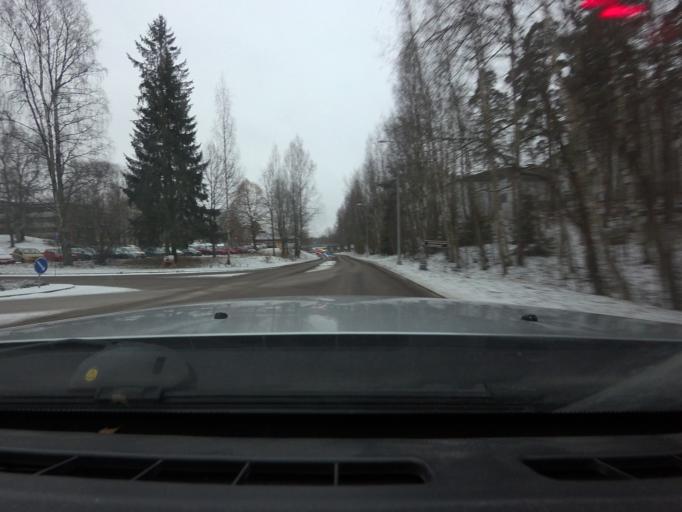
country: FI
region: Uusimaa
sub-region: Helsinki
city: Kauniainen
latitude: 60.2287
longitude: 24.7408
